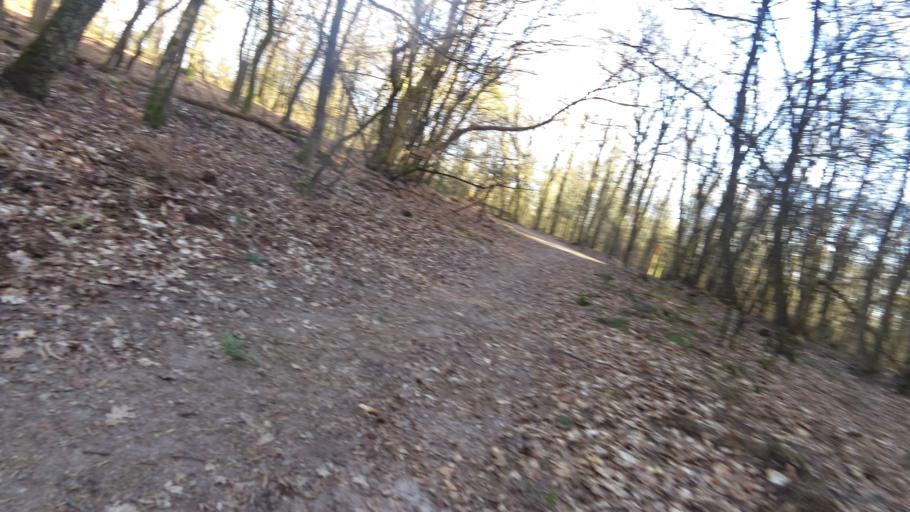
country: NL
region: Gelderland
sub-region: Gemeente Barneveld
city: Garderen
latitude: 52.2743
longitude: 5.6956
